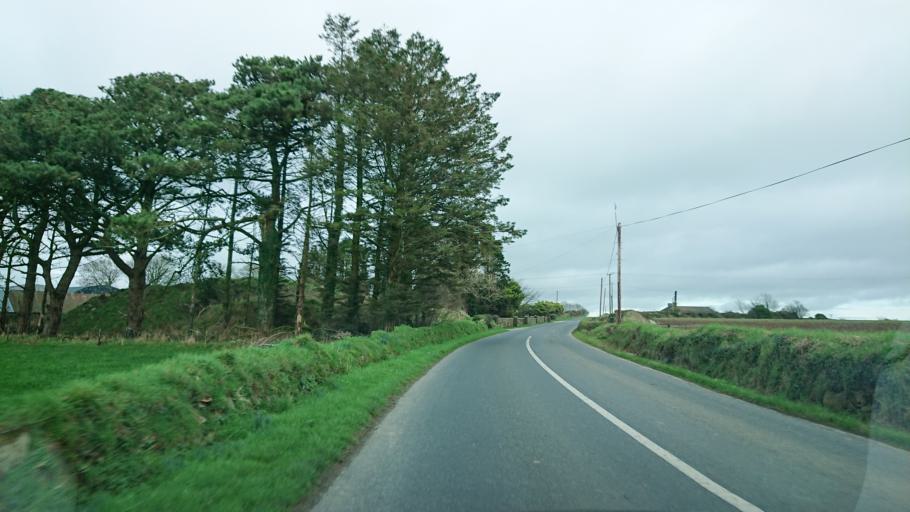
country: IE
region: Munster
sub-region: Waterford
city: Portlaw
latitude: 52.1857
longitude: -7.2948
